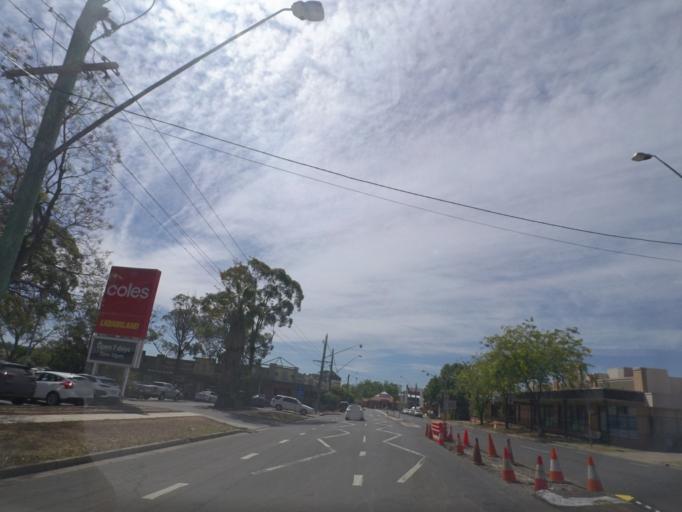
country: AU
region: New South Wales
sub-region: Camden
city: Elderslie
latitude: -34.0569
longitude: 150.6942
